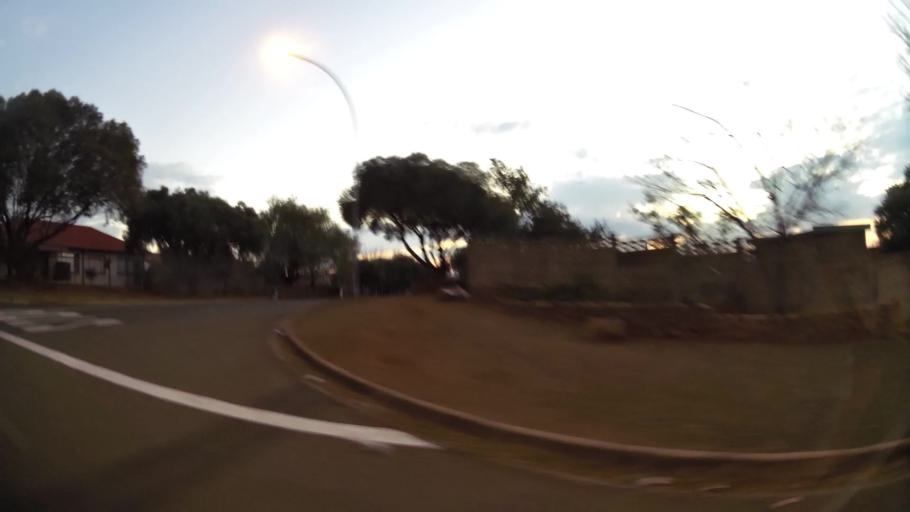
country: ZA
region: Orange Free State
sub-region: Mangaung Metropolitan Municipality
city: Bloemfontein
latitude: -29.1556
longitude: 26.1935
